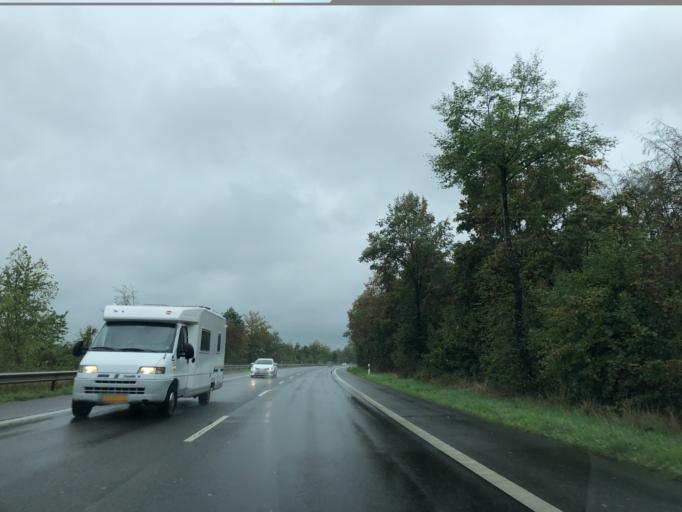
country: DE
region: North Rhine-Westphalia
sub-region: Regierungsbezirk Dusseldorf
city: Grevenbroich
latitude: 51.0759
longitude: 6.5577
